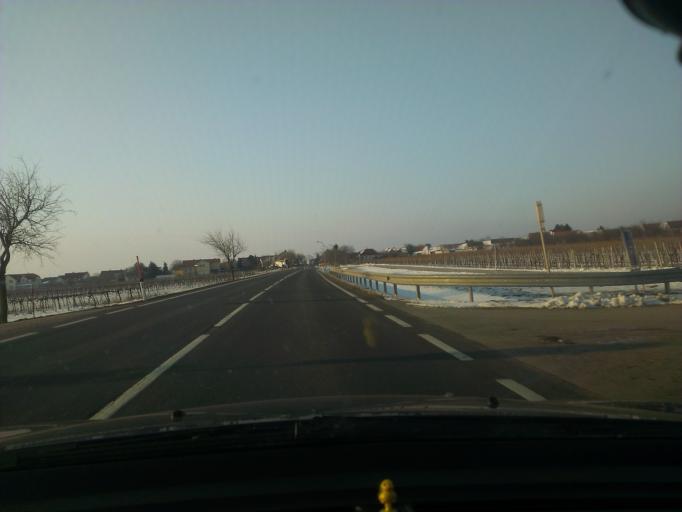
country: AT
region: Burgenland
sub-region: Eisenstadt-Umgebung
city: Donnerskirchen
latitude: 47.8980
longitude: 16.6512
